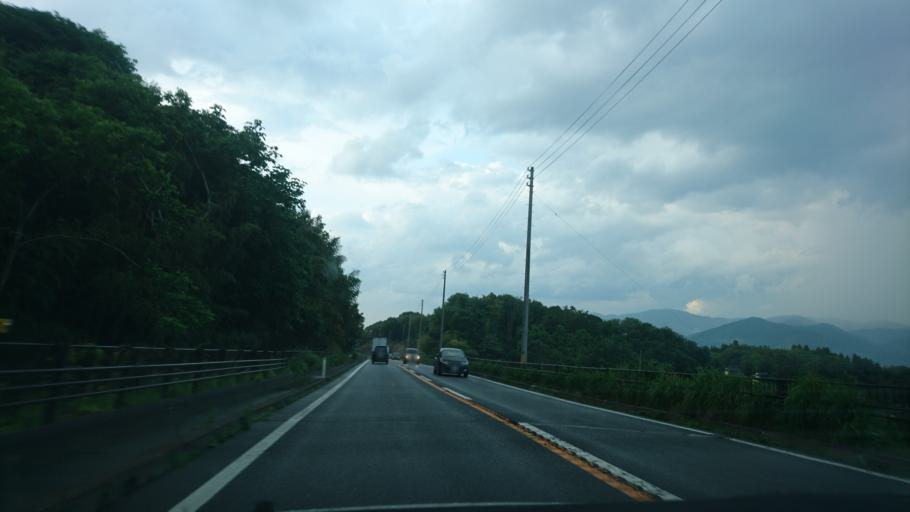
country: JP
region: Iwate
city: Ichinoseki
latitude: 38.9547
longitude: 141.1221
